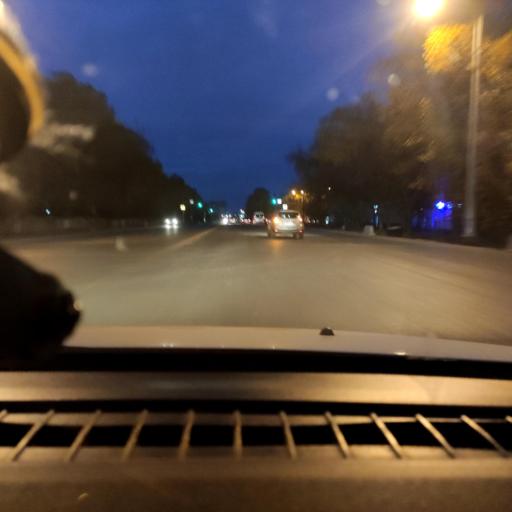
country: RU
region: Samara
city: Samara
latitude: 53.1201
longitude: 50.0868
